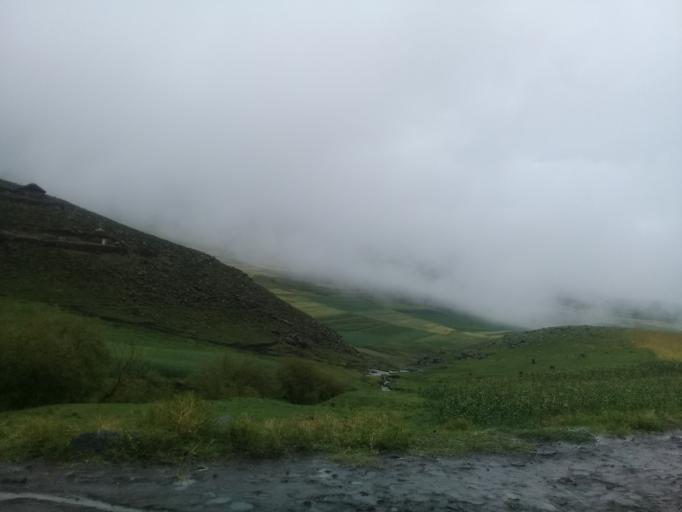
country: LS
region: Mokhotlong
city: Mokhotlong
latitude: -29.3851
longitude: 28.9798
